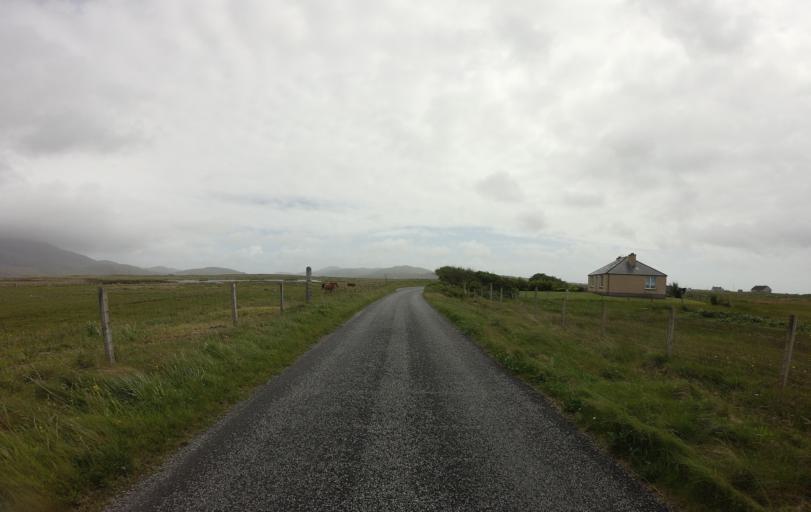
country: GB
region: Scotland
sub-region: Eilean Siar
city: Isle of South Uist
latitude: 57.2568
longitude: -7.4050
